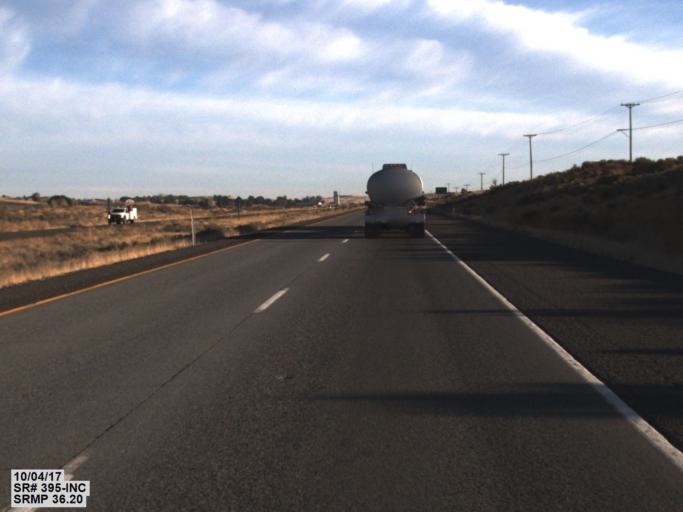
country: US
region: Washington
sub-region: Franklin County
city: Basin City
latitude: 46.4320
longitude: -119.0244
